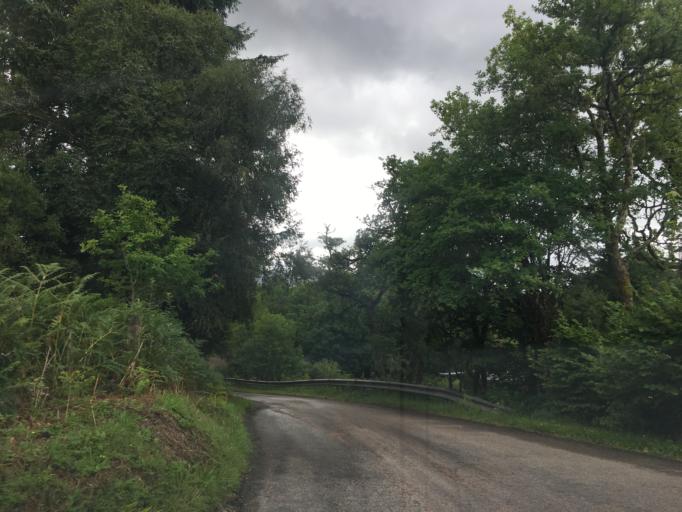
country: GB
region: Scotland
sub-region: Argyll and Bute
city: Oban
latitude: 56.2758
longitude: -5.2788
